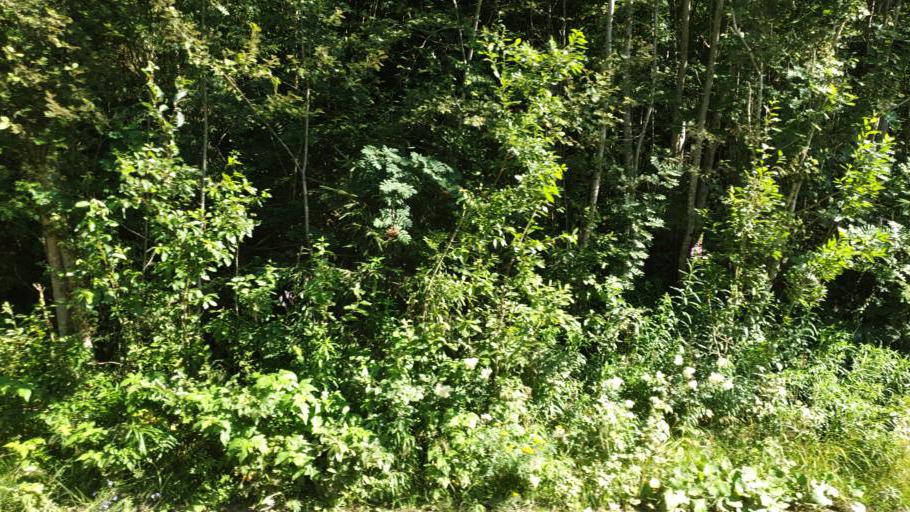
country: NO
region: Sor-Trondelag
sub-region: Orkdal
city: Orkanger
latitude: 63.1900
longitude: 9.7801
